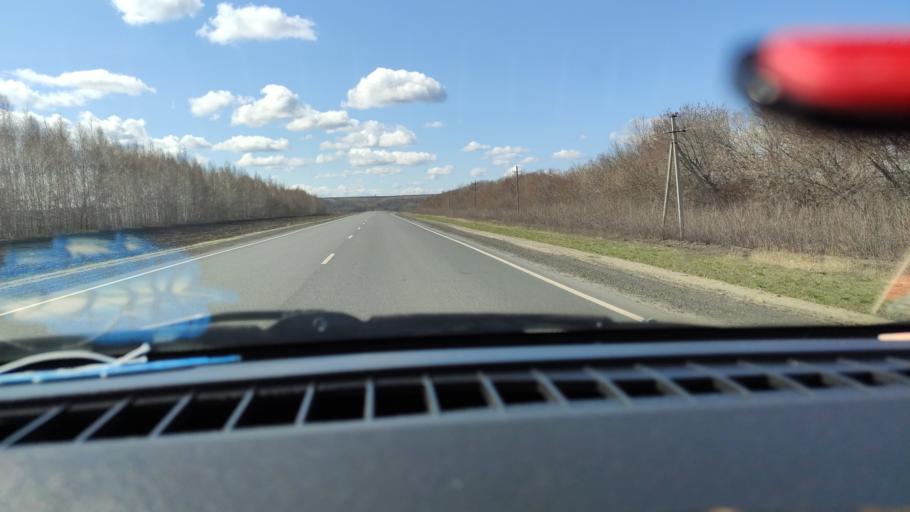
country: RU
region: Samara
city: Syzran'
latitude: 52.9778
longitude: 48.3109
